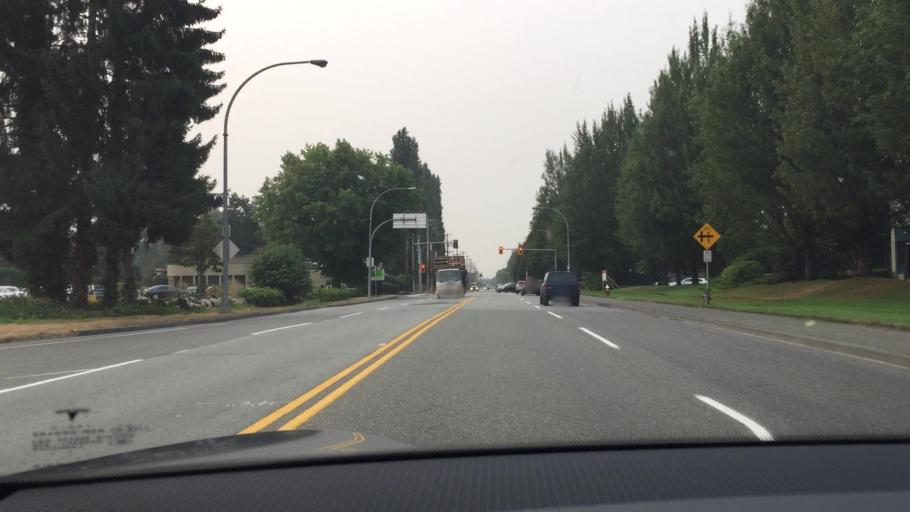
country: CA
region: British Columbia
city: Richmond
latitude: 49.1776
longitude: -123.0693
